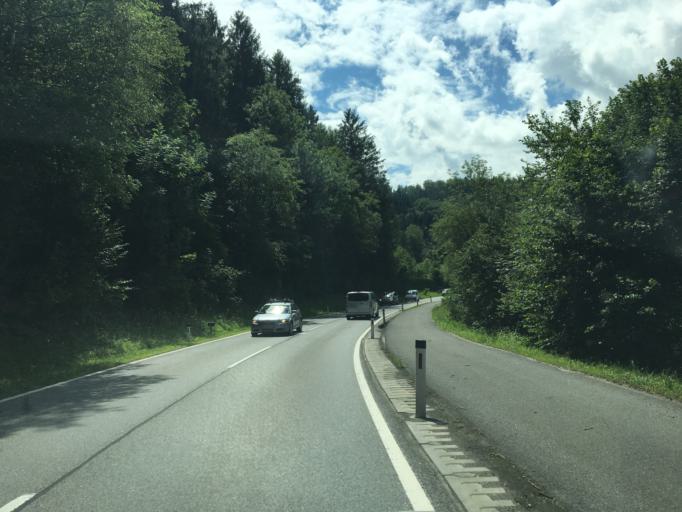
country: AT
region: Salzburg
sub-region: Politischer Bezirk Hallein
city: Adnet
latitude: 47.7000
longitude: 13.1221
